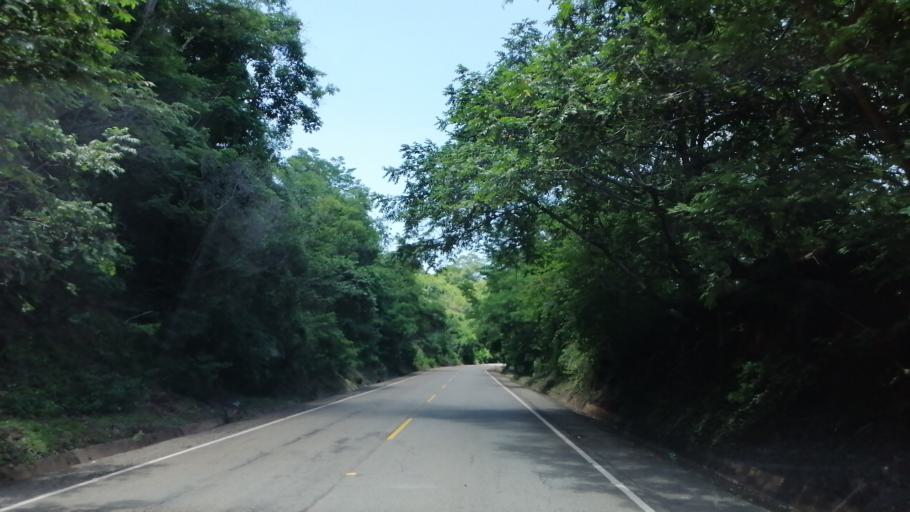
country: SV
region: Chalatenango
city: Nueva Concepcion
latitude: 14.1776
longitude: -89.3190
